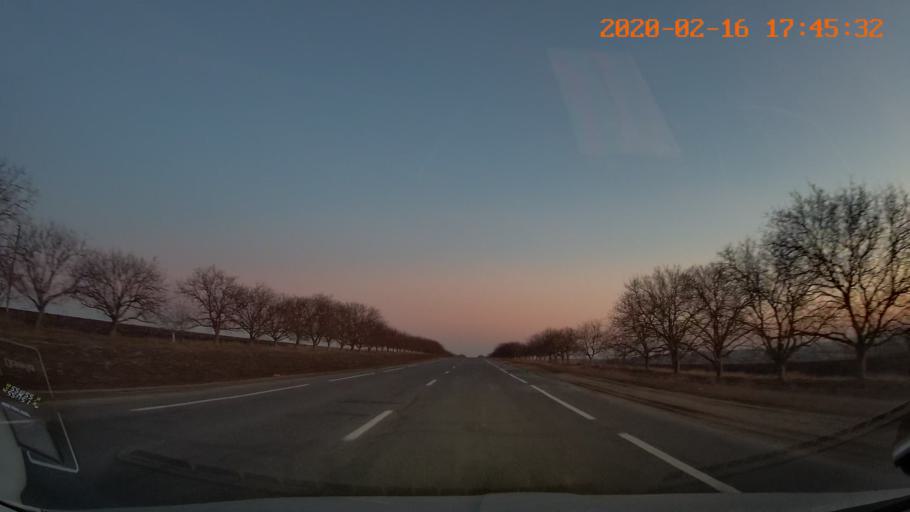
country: MD
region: Riscani
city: Riscani
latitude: 47.9826
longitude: 27.5808
